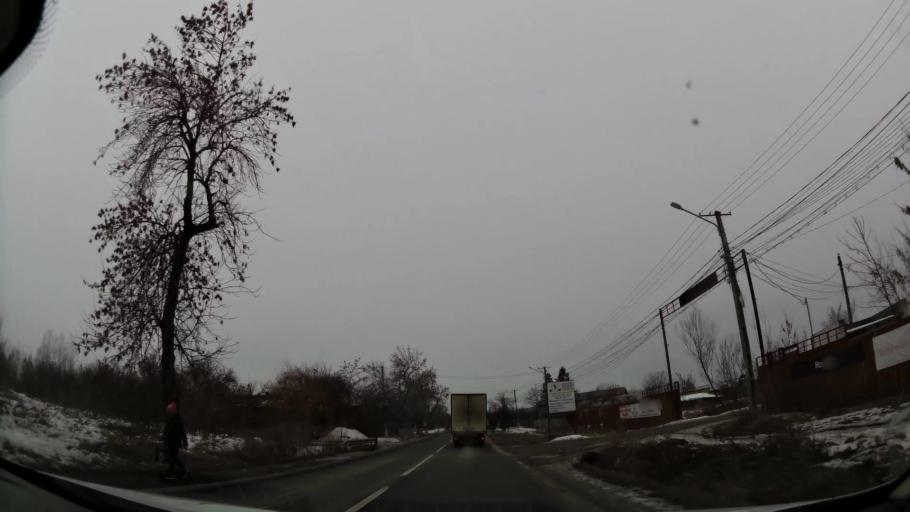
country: RO
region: Dambovita
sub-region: Comuna Tartasesti
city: Baldana
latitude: 44.6032
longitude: 25.7744
